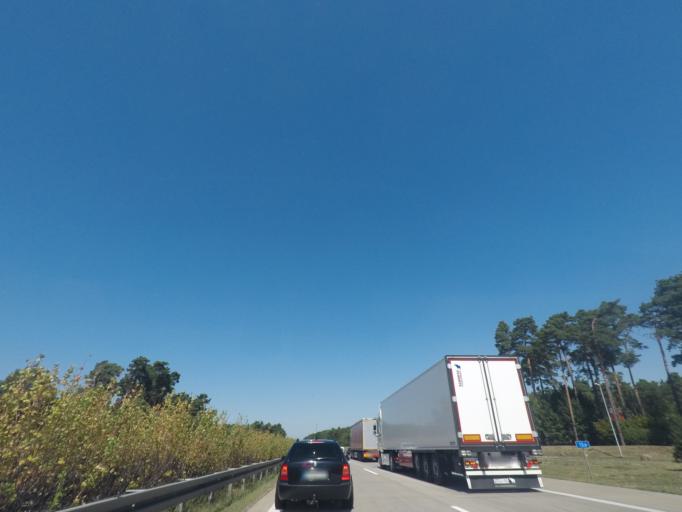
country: DE
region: Brandenburg
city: Bestensee
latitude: 52.2081
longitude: 13.6086
